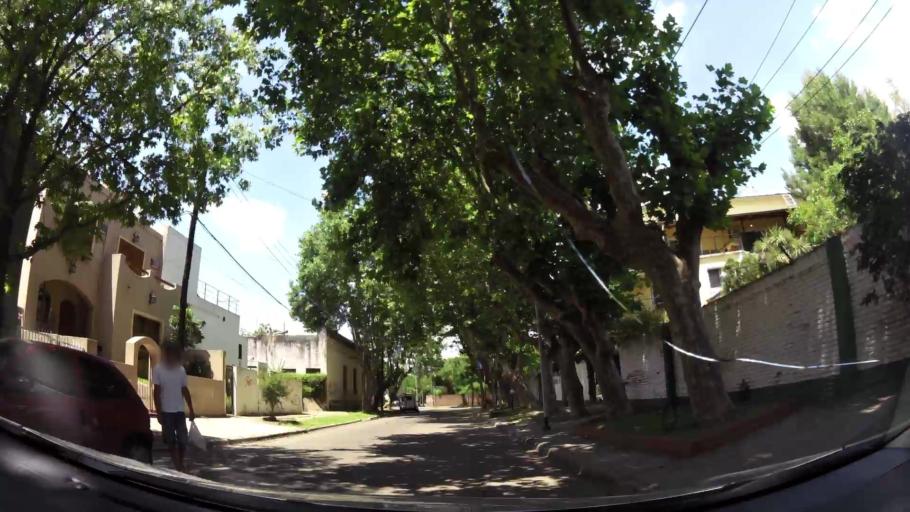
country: AR
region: Buenos Aires
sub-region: Partido de Tigre
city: Tigre
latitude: -34.4147
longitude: -58.5882
